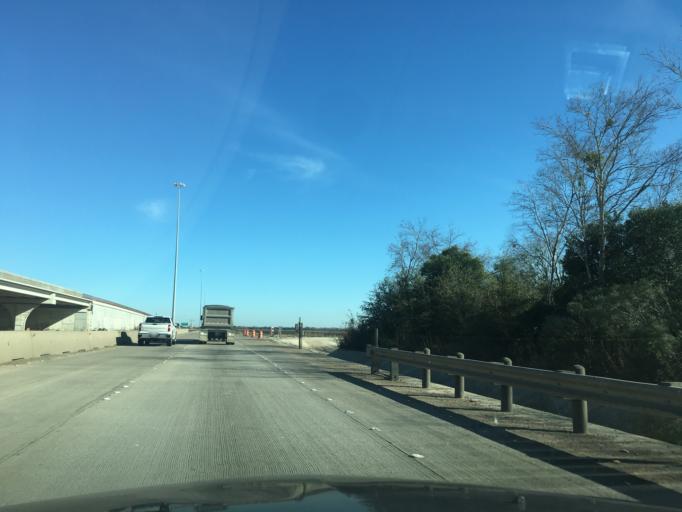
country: US
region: Texas
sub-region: Fort Bend County
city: Rosenberg
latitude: 29.5342
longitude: -95.8467
